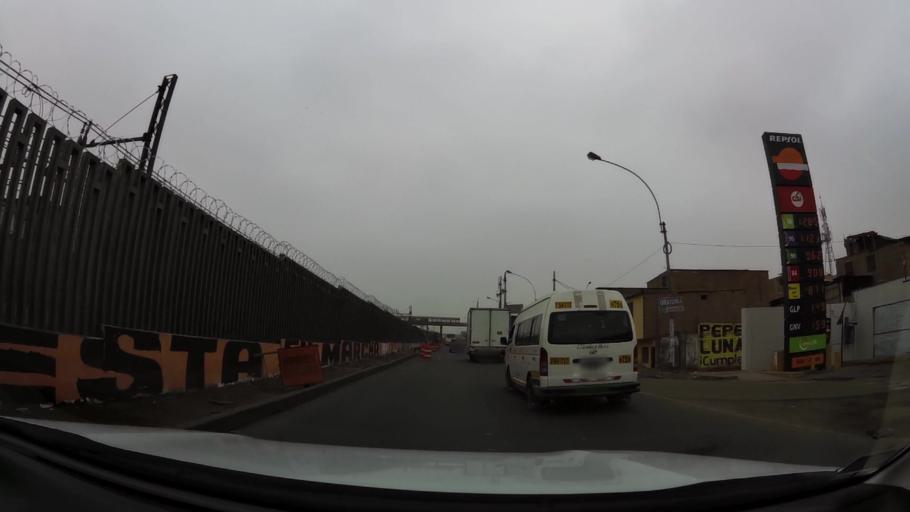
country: PE
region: Lima
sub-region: Lima
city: Surco
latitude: -12.1634
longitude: -76.9546
